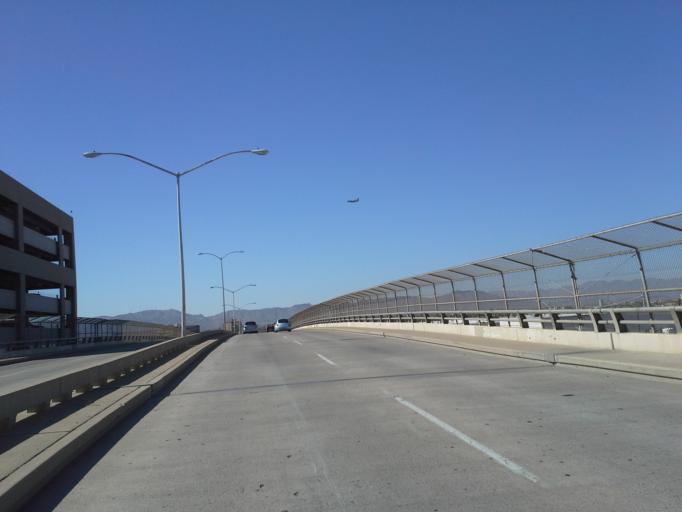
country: US
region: Arizona
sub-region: Maricopa County
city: Phoenix
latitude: 33.4451
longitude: -112.0825
